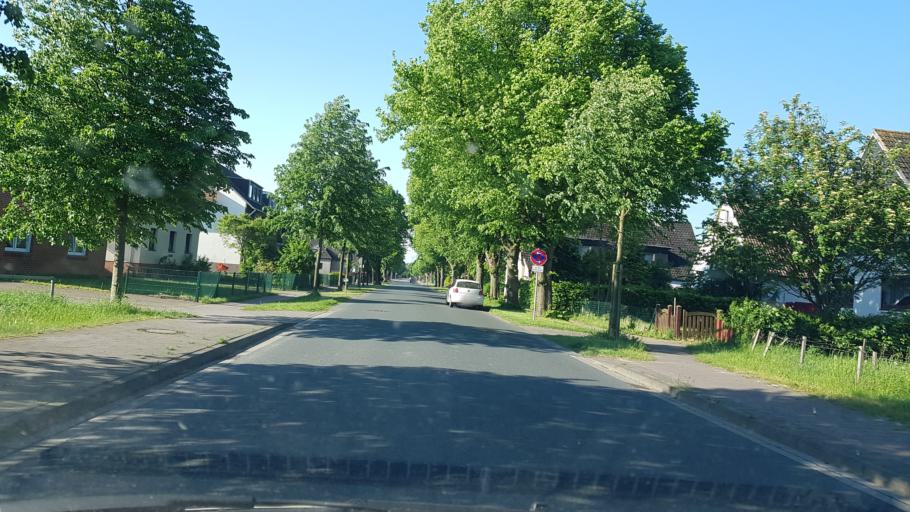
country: DE
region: Lower Saxony
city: Wremen
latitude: 53.6090
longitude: 8.5364
